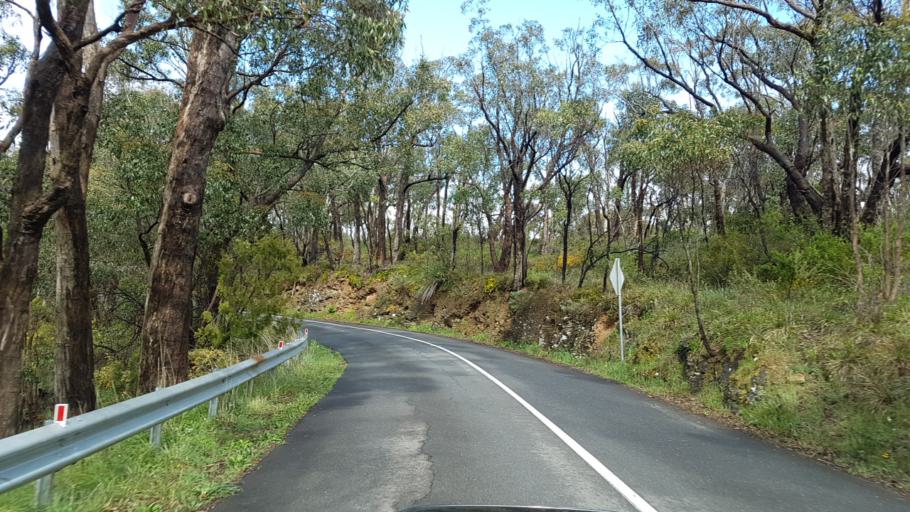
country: AU
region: South Australia
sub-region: Adelaide Hills
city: Adelaide Hills
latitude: -34.9107
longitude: 138.7579
